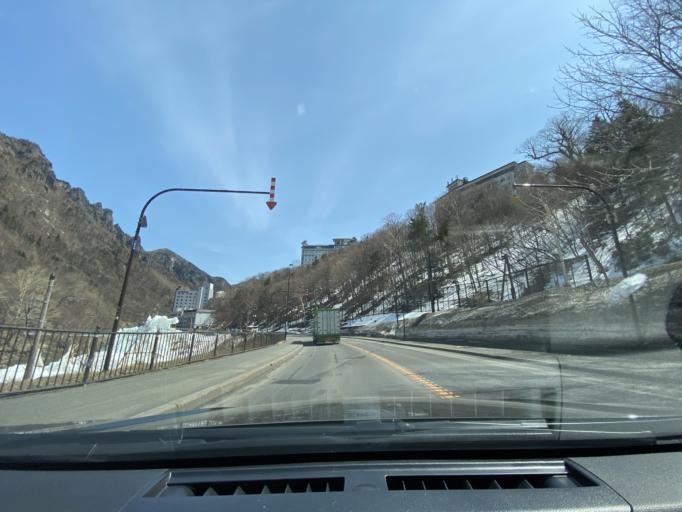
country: JP
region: Hokkaido
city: Kamikawa
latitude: 43.7268
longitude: 142.9486
